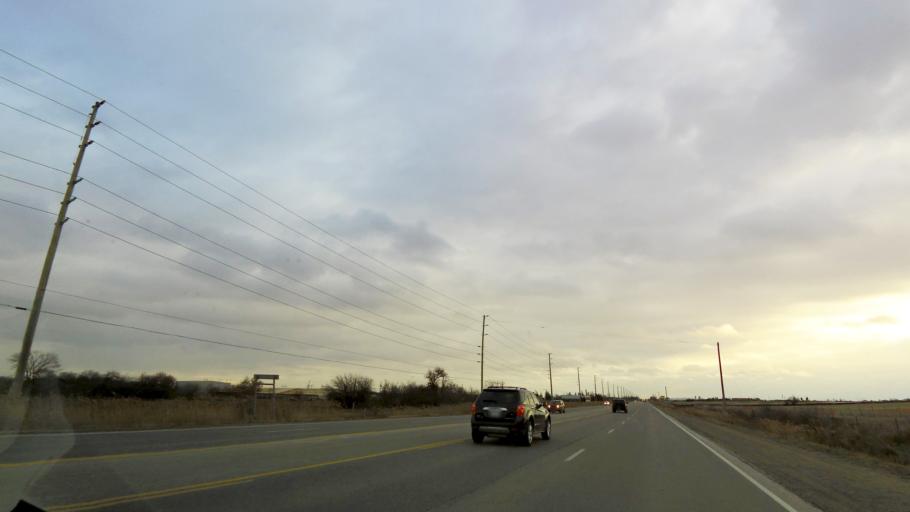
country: CA
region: Ontario
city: Brampton
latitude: 43.8337
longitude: -79.6871
